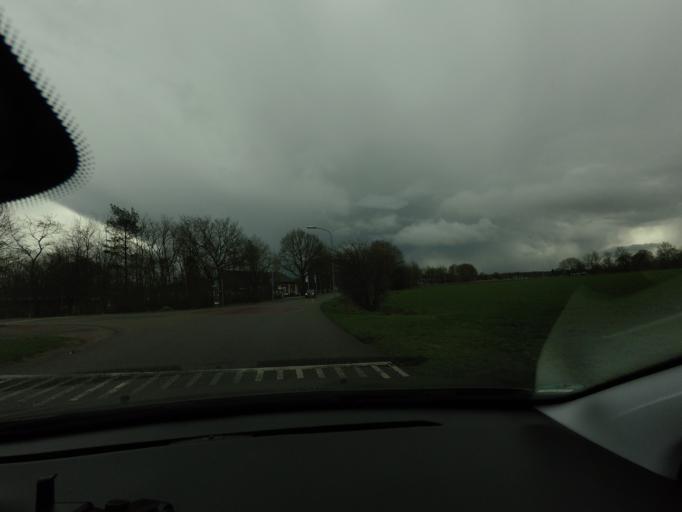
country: NL
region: Drenthe
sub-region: Gemeente Borger-Odoorn
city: Borger
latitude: 52.9778
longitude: 6.7913
